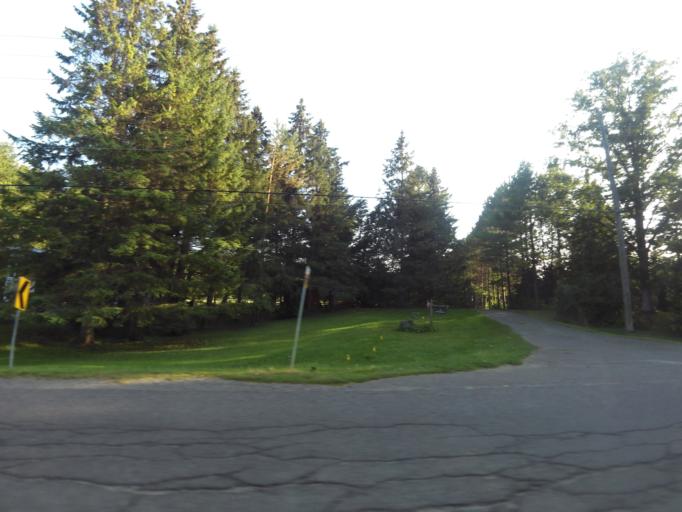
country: CA
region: Ontario
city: Clarence-Rockland
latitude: 45.5016
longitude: -75.3981
